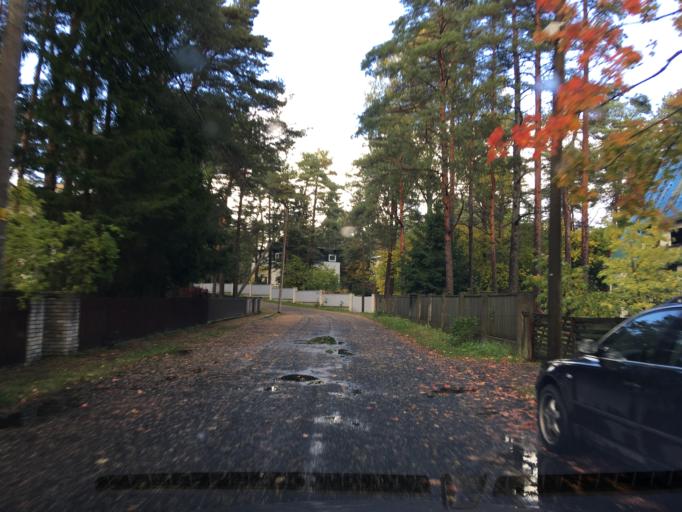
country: EE
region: Harju
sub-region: Tallinna linn
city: Tallinn
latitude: 59.3801
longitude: 24.7118
